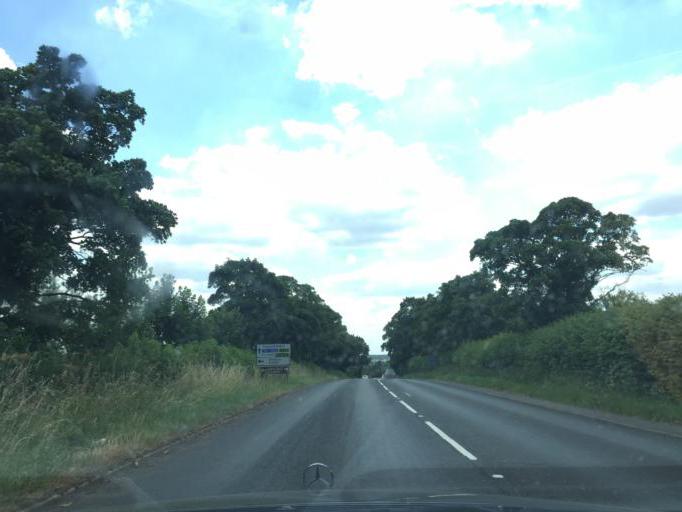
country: GB
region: England
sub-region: Warwickshire
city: Bedworth
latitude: 52.4518
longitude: -1.4092
